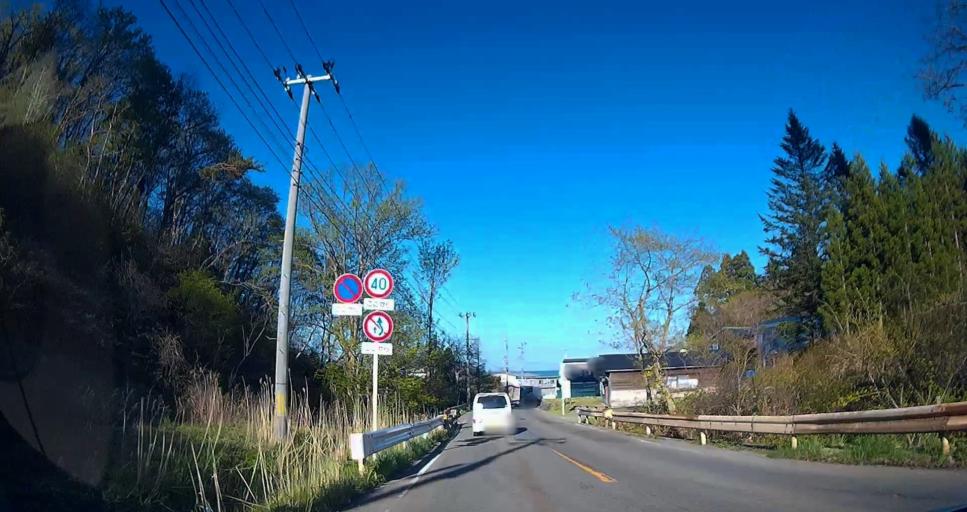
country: JP
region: Aomori
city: Mutsu
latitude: 41.4215
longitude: 141.1490
